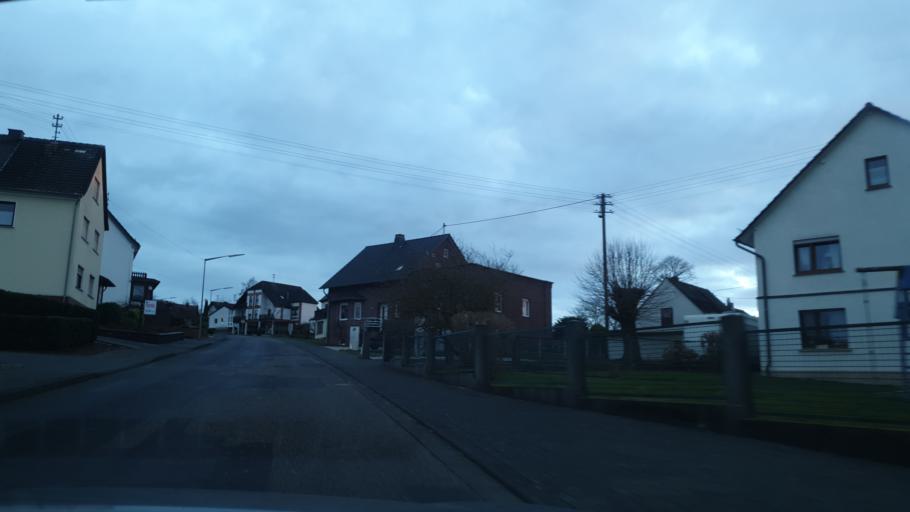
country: DE
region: Rheinland-Pfalz
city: Fluterschen
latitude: 50.6704
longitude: 7.6282
